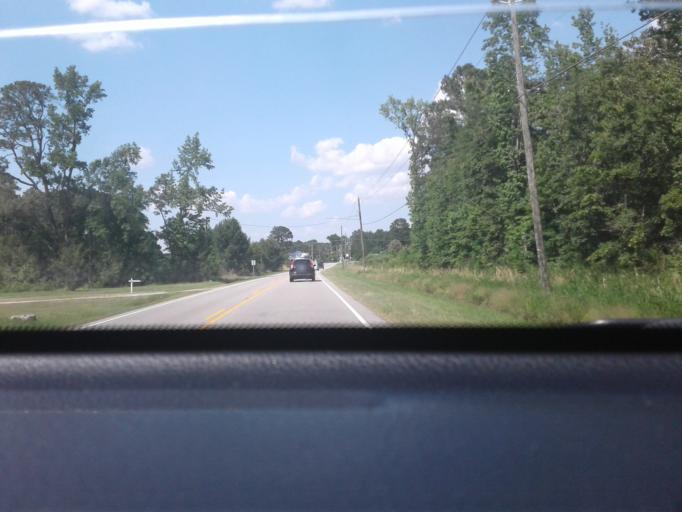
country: US
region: North Carolina
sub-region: Harnett County
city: Erwin
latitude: 35.2136
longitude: -78.6800
